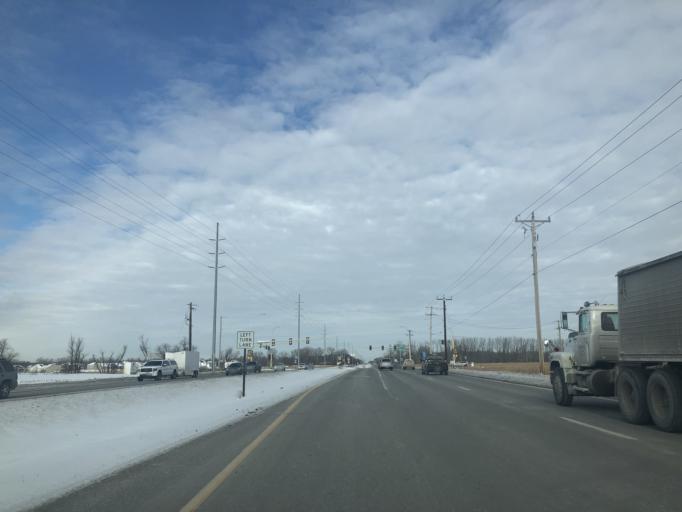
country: US
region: Minnesota
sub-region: Anoka County
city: Circle Pines
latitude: 45.1664
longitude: -93.1630
